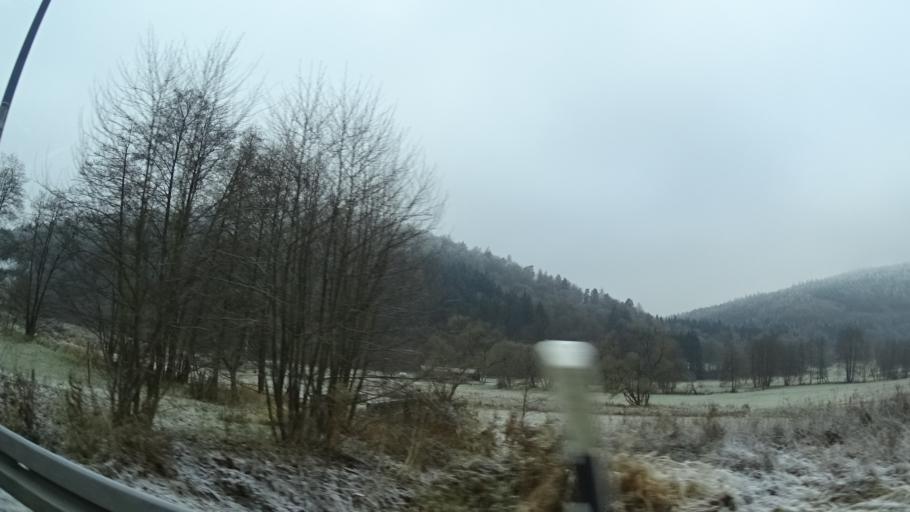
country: DE
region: Bavaria
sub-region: Regierungsbezirk Unterfranken
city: Zeitlofs
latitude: 50.2739
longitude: 9.7133
